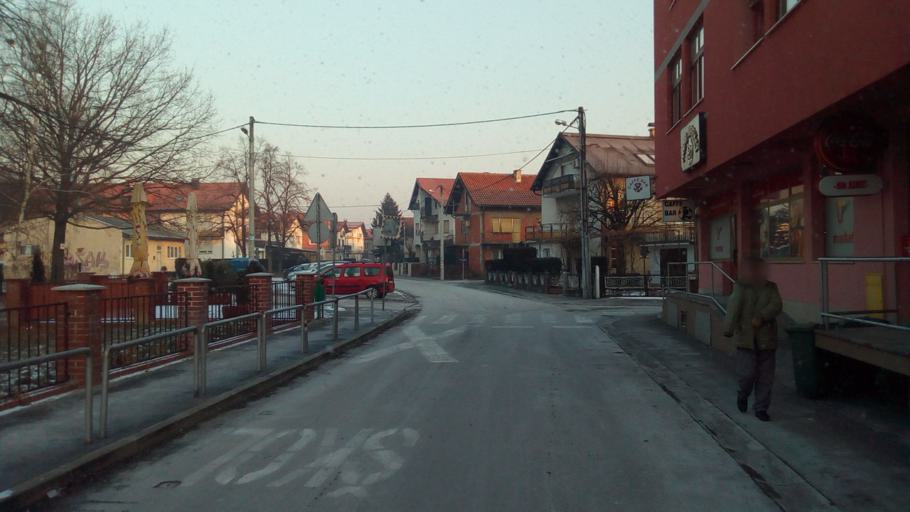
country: HR
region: Grad Zagreb
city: Dubrava
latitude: 45.8101
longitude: 16.0480
